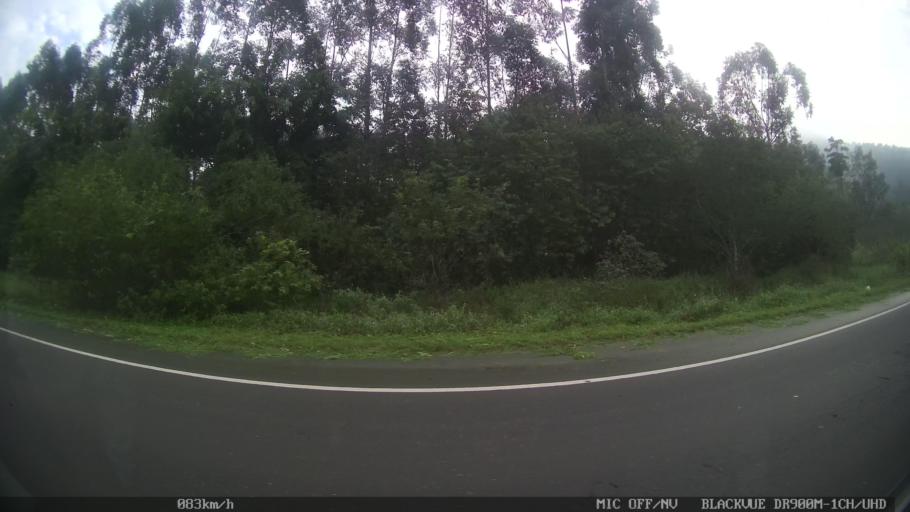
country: BR
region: Santa Catarina
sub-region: Penha
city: Penha
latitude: -26.8092
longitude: -48.6714
